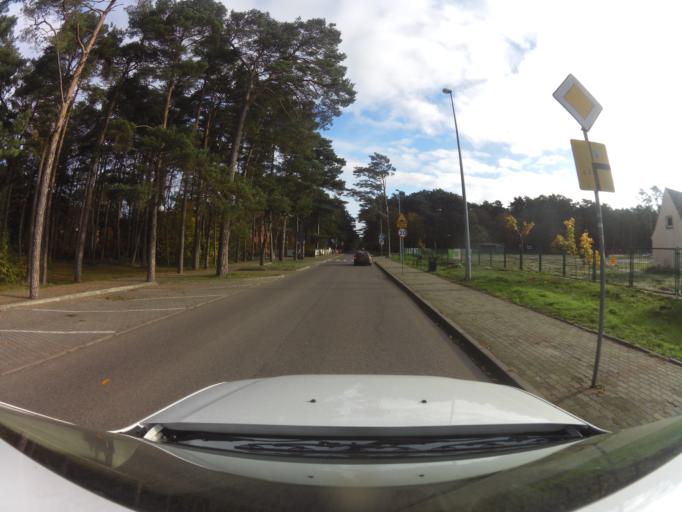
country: PL
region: West Pomeranian Voivodeship
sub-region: Powiat gryficki
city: Cerkwica
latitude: 54.1028
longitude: 15.1193
